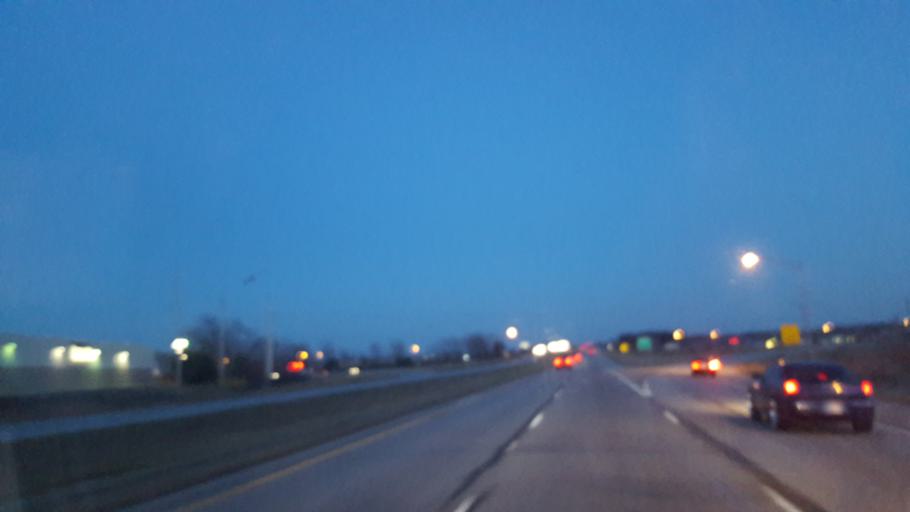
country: US
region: Indiana
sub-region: Kosciusko County
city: Warsaw
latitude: 41.2679
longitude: -85.8582
